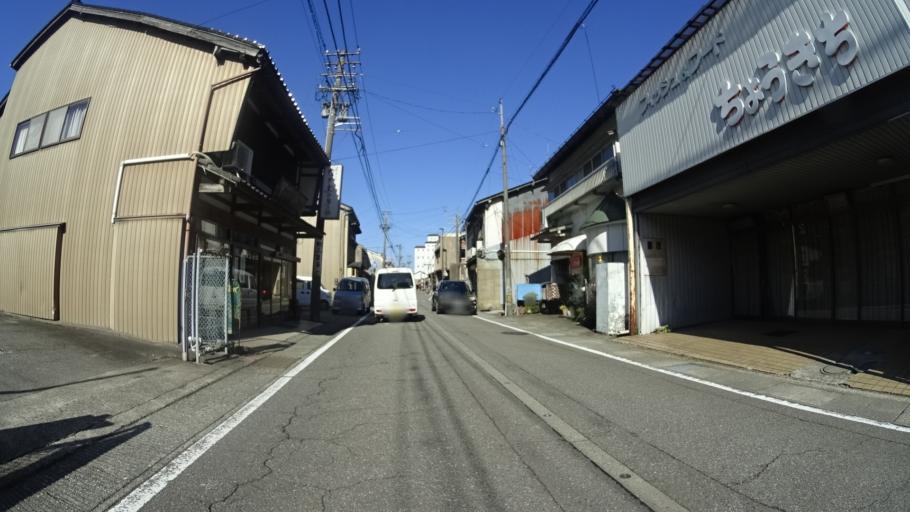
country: JP
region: Ishikawa
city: Tsurugi-asahimachi
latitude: 36.4440
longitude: 136.6303
